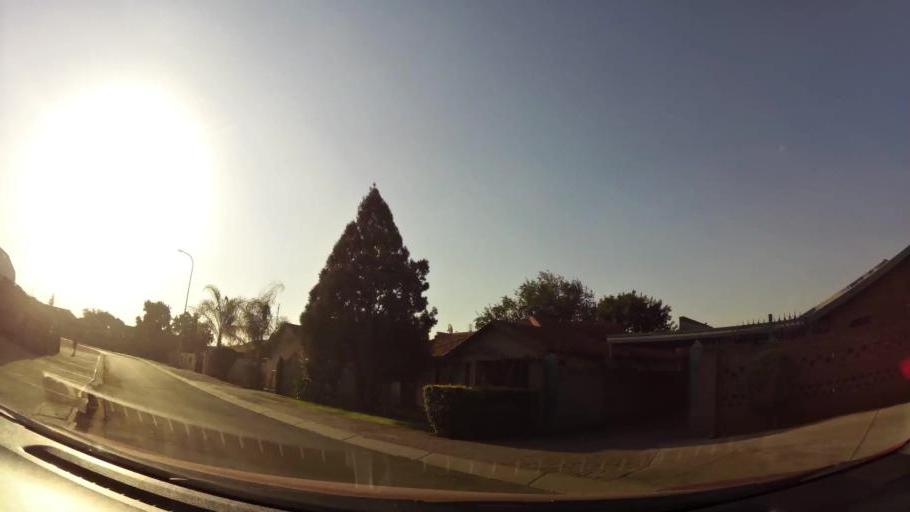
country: ZA
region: North-West
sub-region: Bojanala Platinum District Municipality
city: Rustenburg
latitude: -25.6502
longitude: 27.2215
